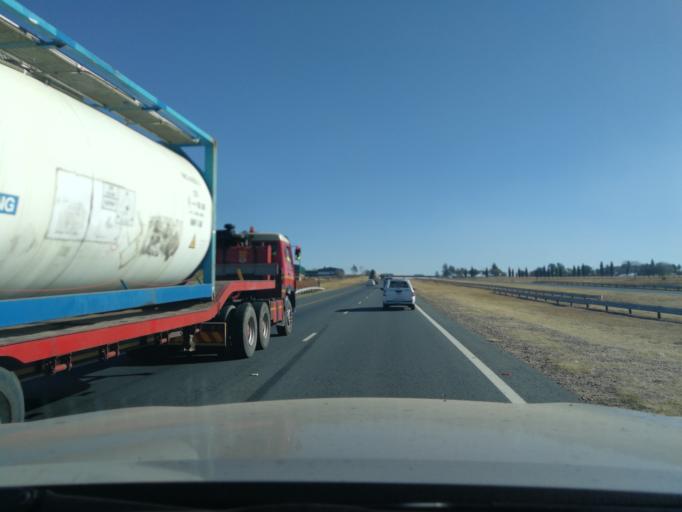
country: ZA
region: Gauteng
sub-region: West Rand District Municipality
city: Muldersdriseloop
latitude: -26.0100
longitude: 27.8871
